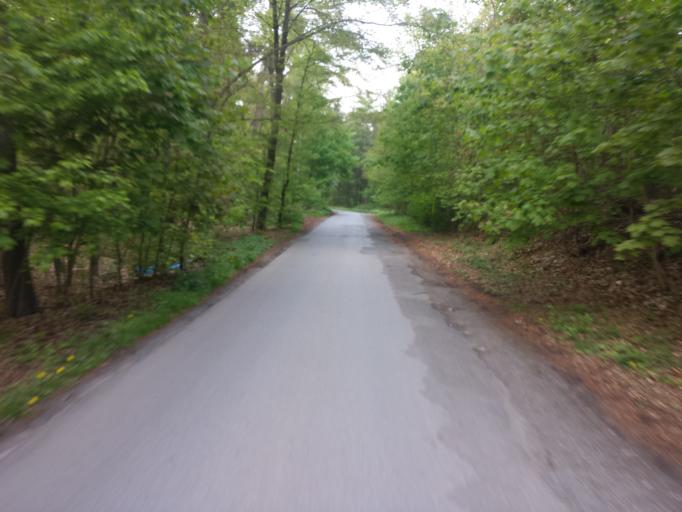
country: DE
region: North Rhine-Westphalia
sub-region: Regierungsbezirk Detmold
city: Guetersloh
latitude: 51.8920
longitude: 8.3456
